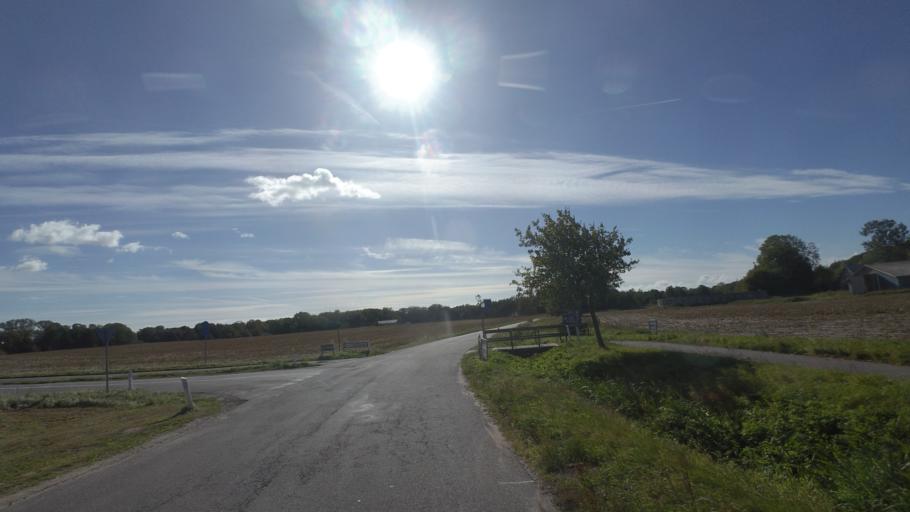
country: DK
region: Capital Region
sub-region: Bornholm Kommune
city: Akirkeby
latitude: 55.0094
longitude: 14.9921
